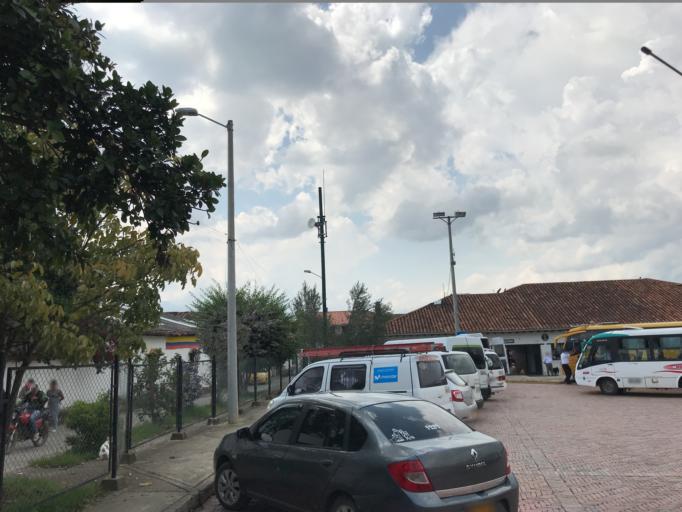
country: CO
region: Boyaca
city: Villa de Leiva
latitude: 5.6303
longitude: -73.5257
